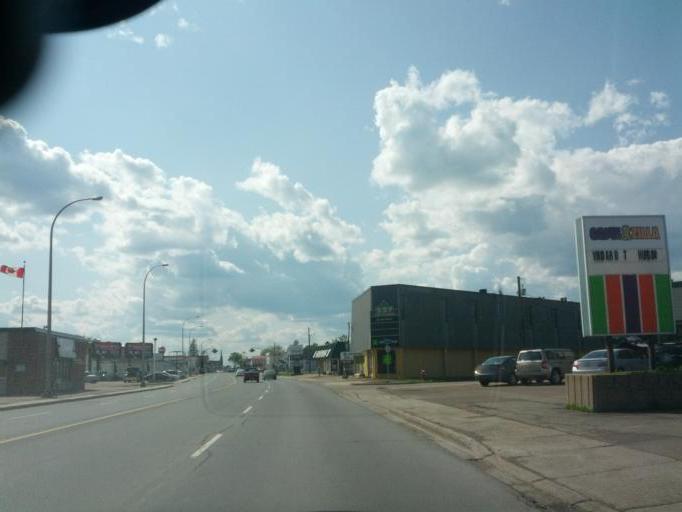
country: CA
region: New Brunswick
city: Moncton
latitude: 46.0977
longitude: -64.7964
